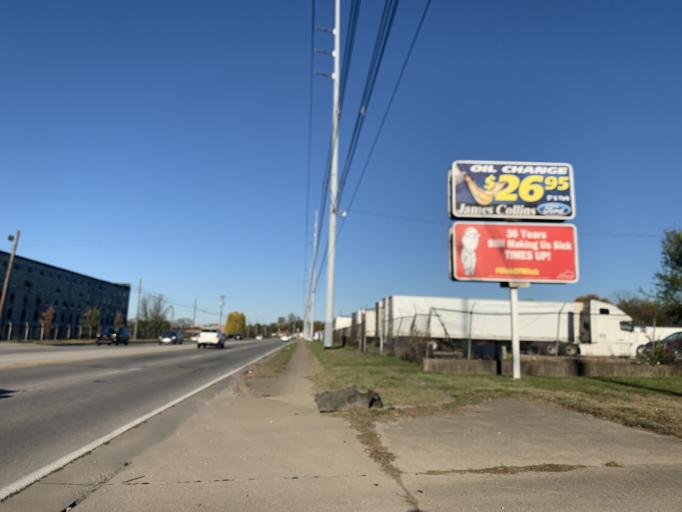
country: US
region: Kentucky
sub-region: Jefferson County
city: Shively
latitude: 38.2004
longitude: -85.7949
